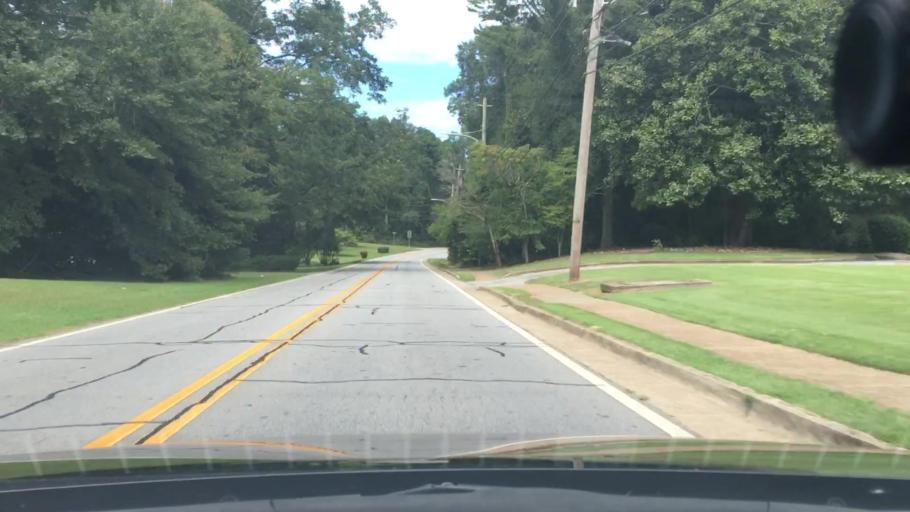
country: US
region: Georgia
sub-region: Coweta County
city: Newnan
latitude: 33.3944
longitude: -84.8002
